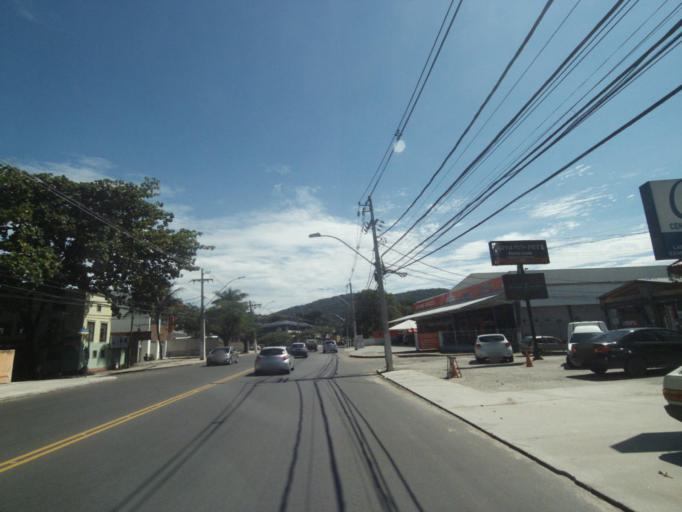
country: BR
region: Rio de Janeiro
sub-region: Niteroi
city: Niteroi
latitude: -22.9457
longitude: -43.0579
